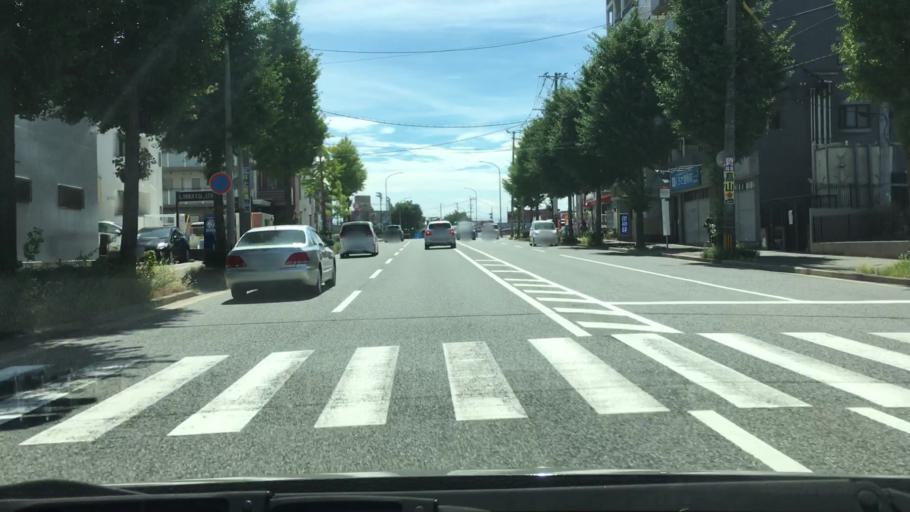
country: JP
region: Fukuoka
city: Fukuoka-shi
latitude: 33.5635
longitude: 130.4318
